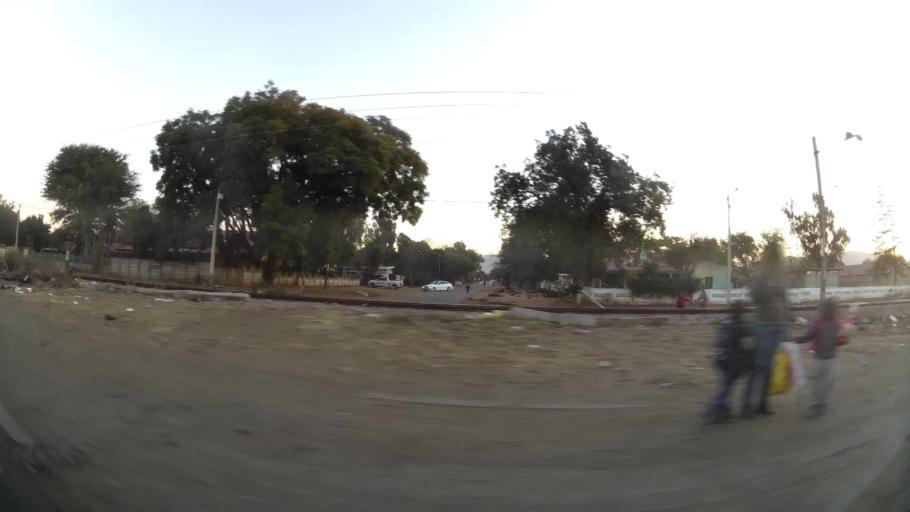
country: ZA
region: North-West
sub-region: Bojanala Platinum District Municipality
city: Rustenburg
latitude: -25.6584
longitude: 27.2461
